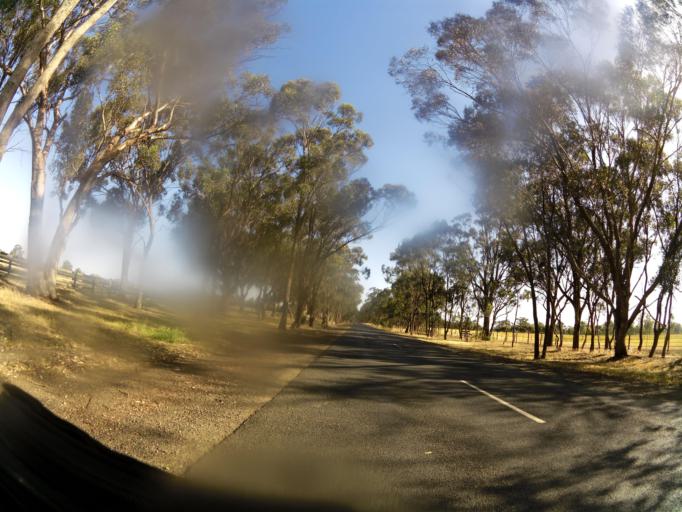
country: AU
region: Victoria
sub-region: Murrindindi
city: Kinglake West
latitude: -36.9691
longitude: 145.1091
